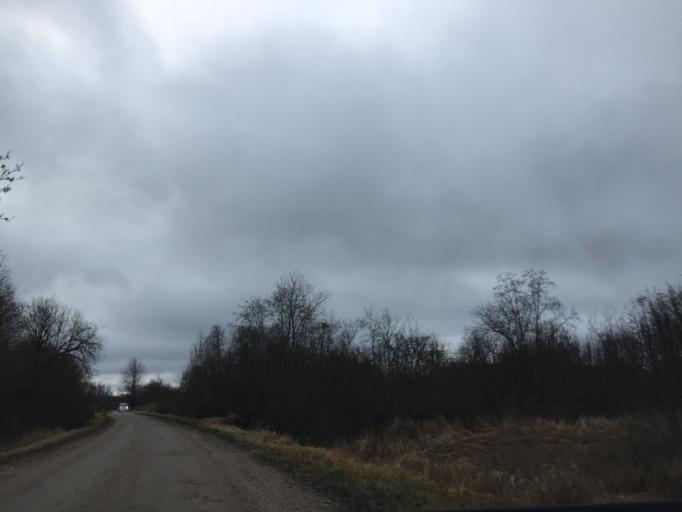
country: LV
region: Broceni
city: Broceni
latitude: 56.6681
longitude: 22.5539
